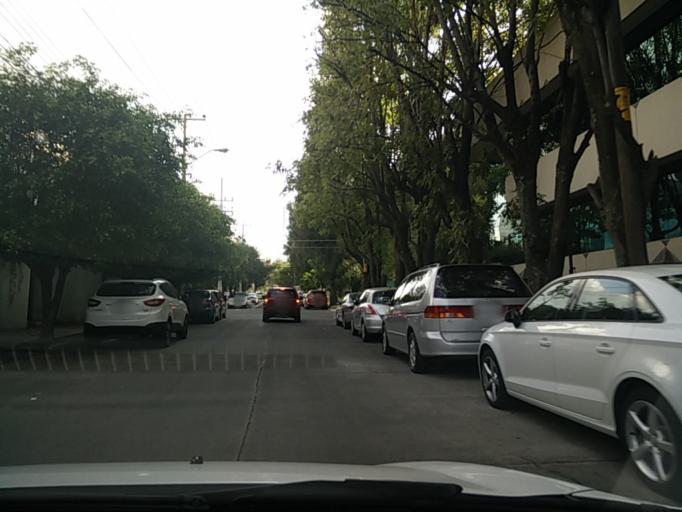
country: MX
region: Jalisco
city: Guadalajara
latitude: 20.6929
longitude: -103.3824
